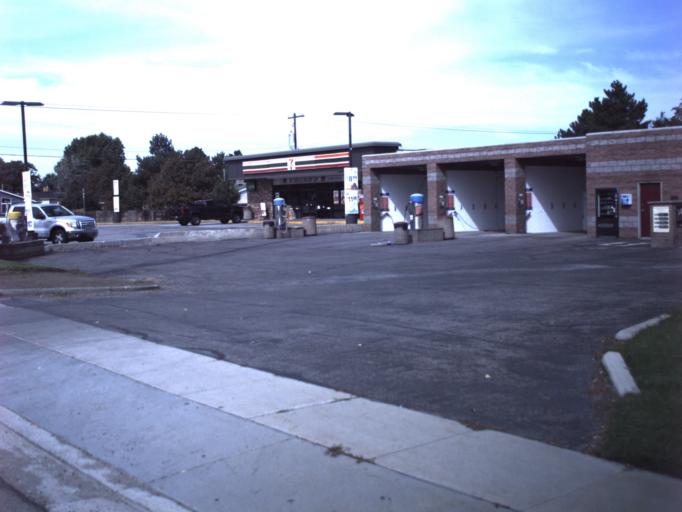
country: US
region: Utah
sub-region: Salt Lake County
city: Kearns
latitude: 40.6532
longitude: -111.9665
